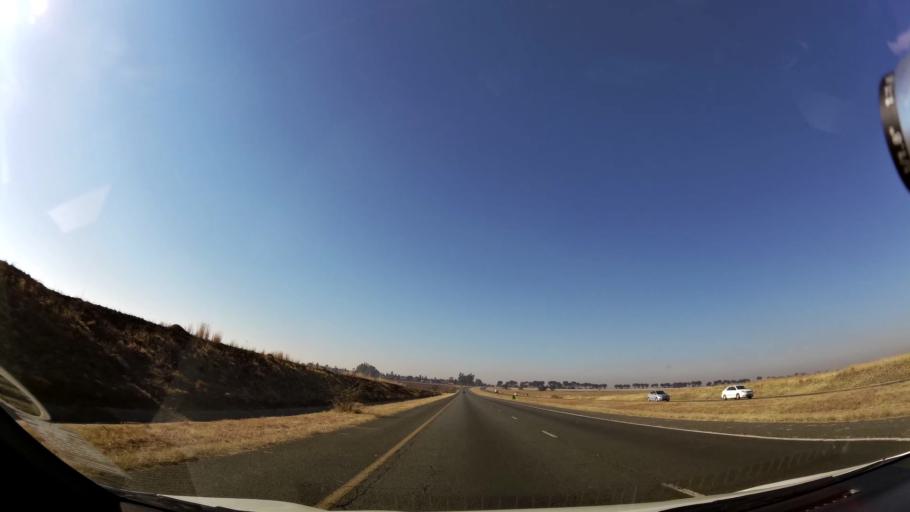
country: ZA
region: Gauteng
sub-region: City of Johannesburg Metropolitan Municipality
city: Johannesburg
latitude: -26.3293
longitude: 28.0735
